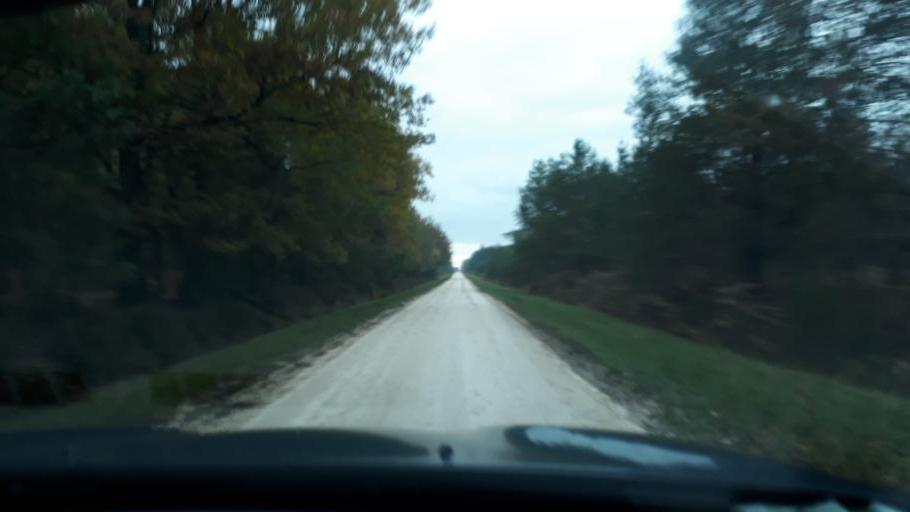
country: FR
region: Centre
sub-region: Departement du Loiret
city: Bouzy-la-Foret
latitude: 47.8436
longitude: 2.4440
